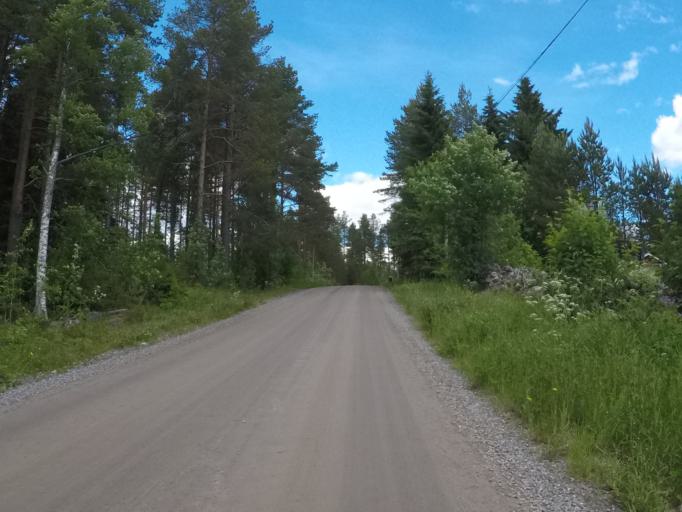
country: SE
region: Vaesterbotten
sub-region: Robertsfors Kommun
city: Robertsfors
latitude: 64.1586
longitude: 20.9191
